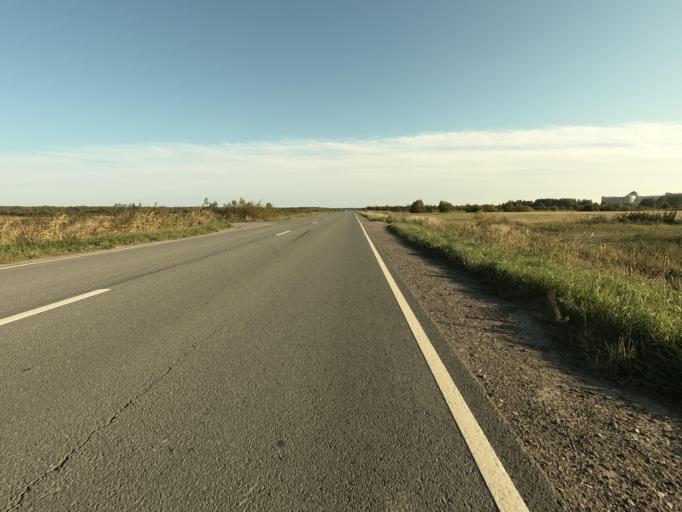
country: RU
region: St.-Petersburg
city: Sapernyy
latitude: 59.7508
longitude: 30.6378
